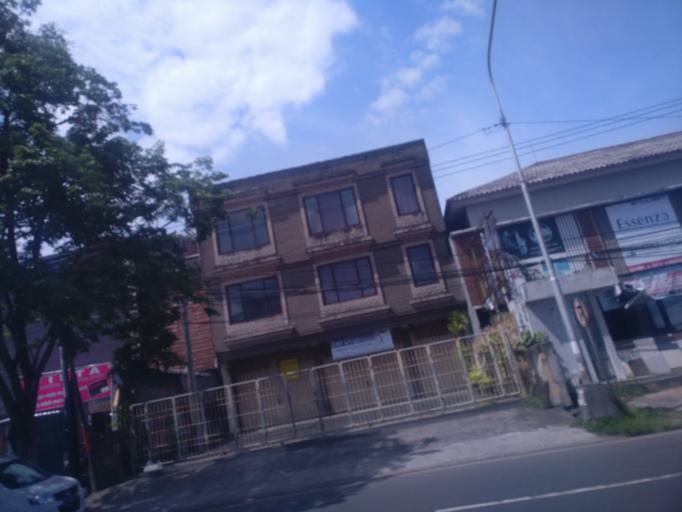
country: ID
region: Bali
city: Banjar Kertasari
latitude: -8.6364
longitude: 115.1911
